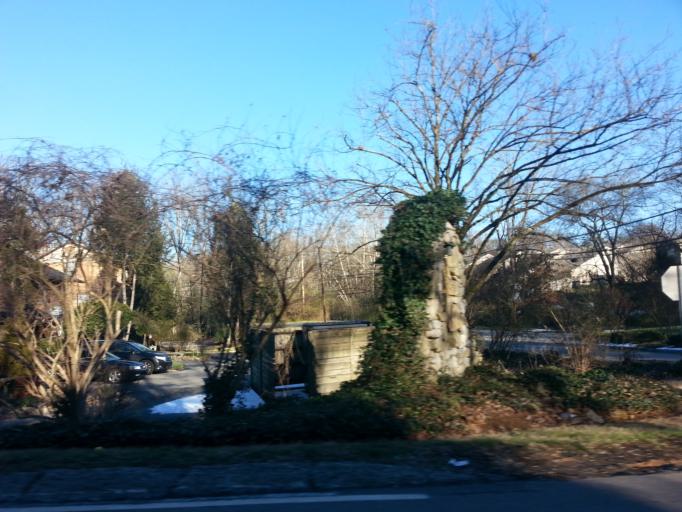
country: US
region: Tennessee
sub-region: Knox County
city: Farragut
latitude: 35.9460
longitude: -84.0567
